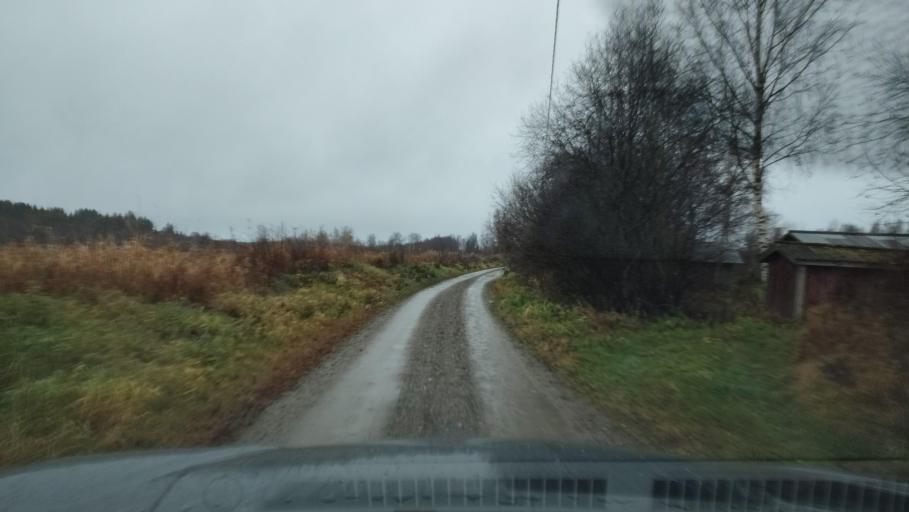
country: FI
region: Ostrobothnia
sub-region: Sydosterbotten
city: Kristinestad
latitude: 62.2298
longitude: 21.4489
